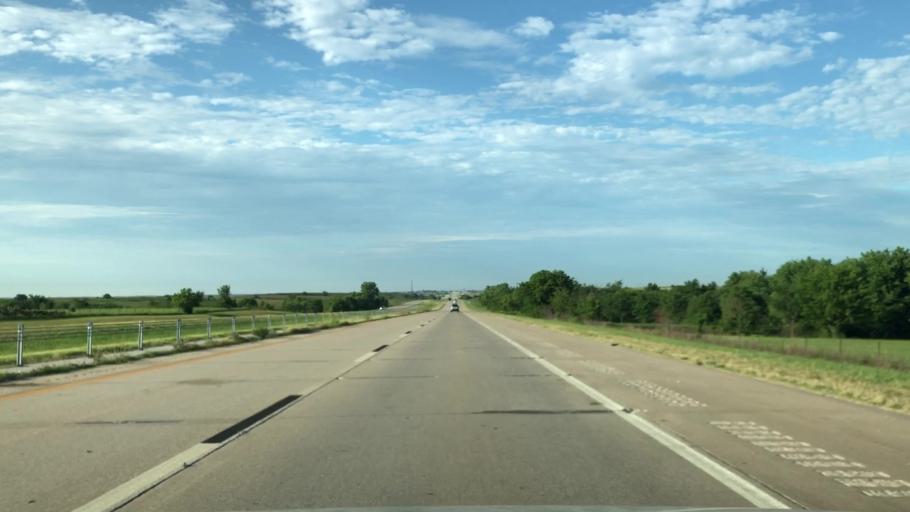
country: US
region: Oklahoma
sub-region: Osage County
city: Skiatook
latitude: 36.4148
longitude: -95.9207
